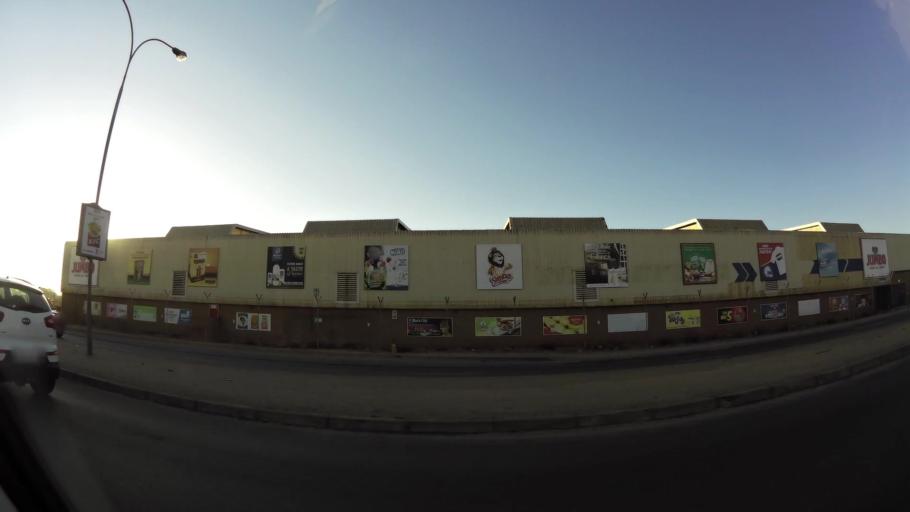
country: ZA
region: Limpopo
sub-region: Capricorn District Municipality
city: Polokwane
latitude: -23.9081
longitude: 29.4410
